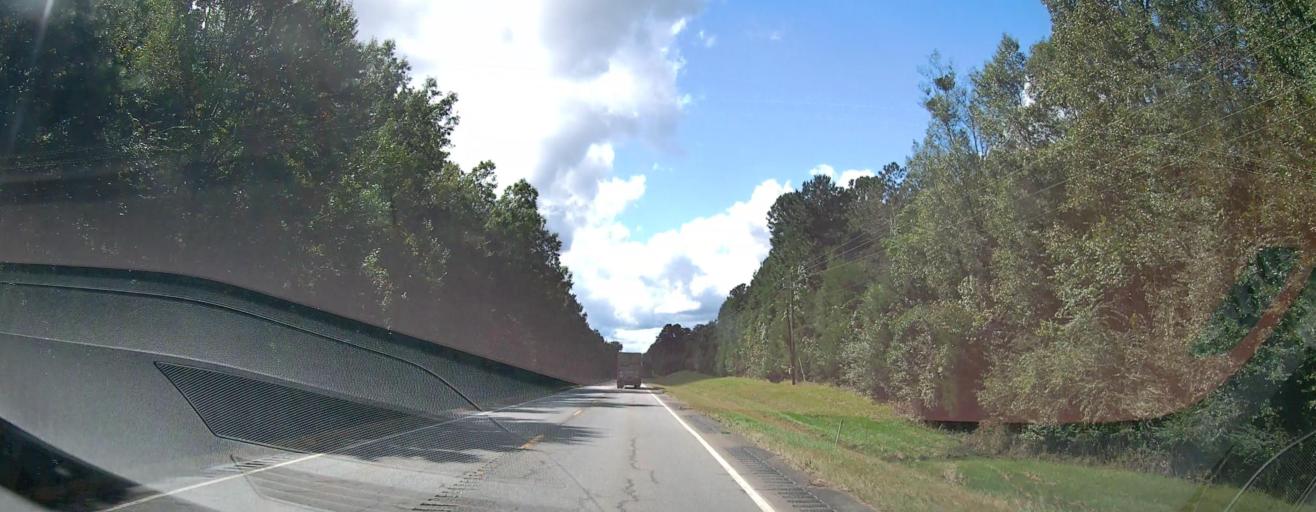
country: US
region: Georgia
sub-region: Jones County
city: Gray
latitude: 33.0213
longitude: -83.4949
